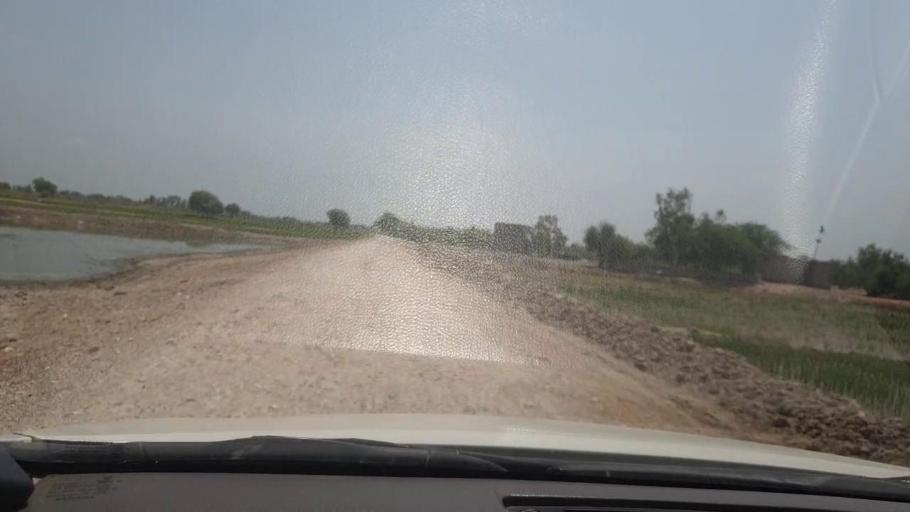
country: PK
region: Sindh
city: Garhi Yasin
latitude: 27.9210
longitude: 68.5524
